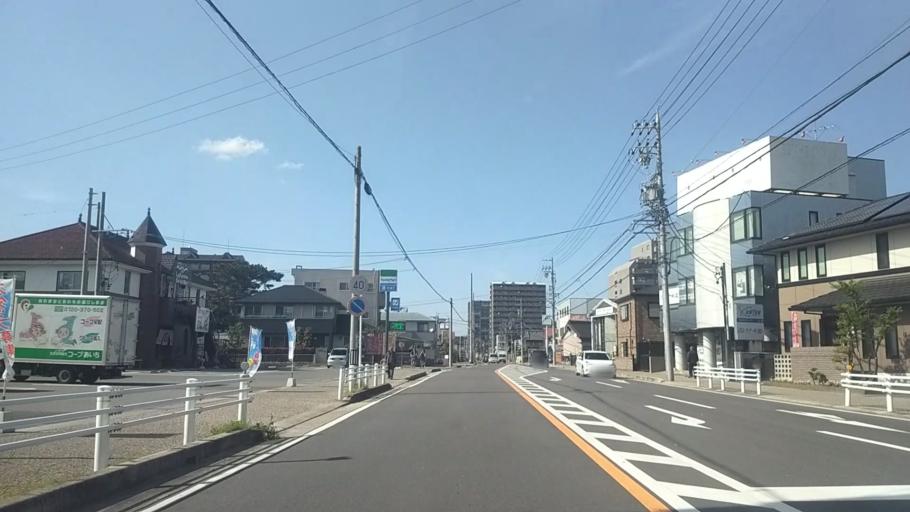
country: JP
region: Aichi
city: Anjo
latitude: 34.9814
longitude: 137.0844
